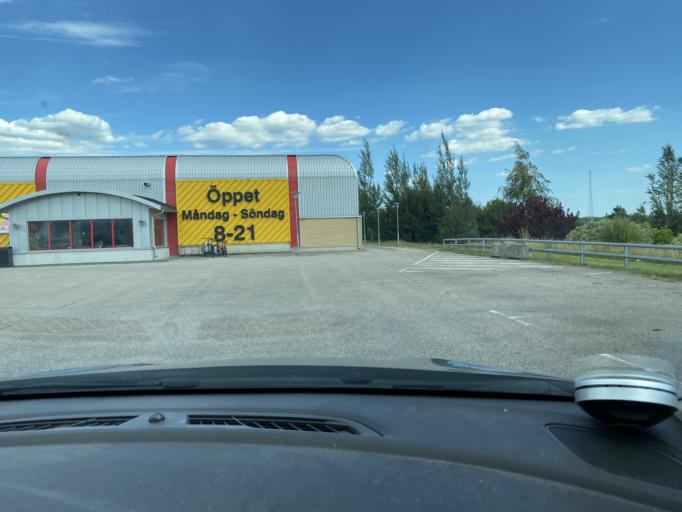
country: SE
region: Kronoberg
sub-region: Markaryds Kommun
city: Markaryd
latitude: 56.4491
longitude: 13.5983
